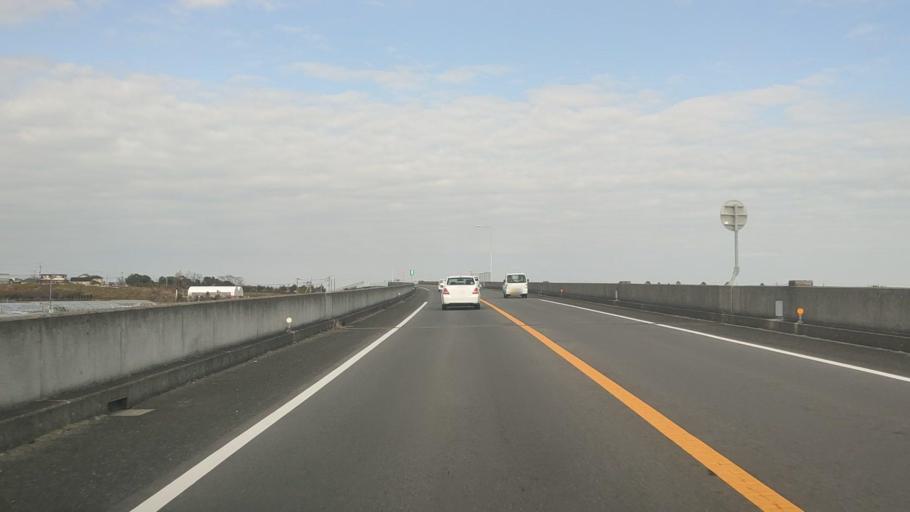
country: JP
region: Nagasaki
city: Shimabara
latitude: 32.7362
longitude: 130.3699
